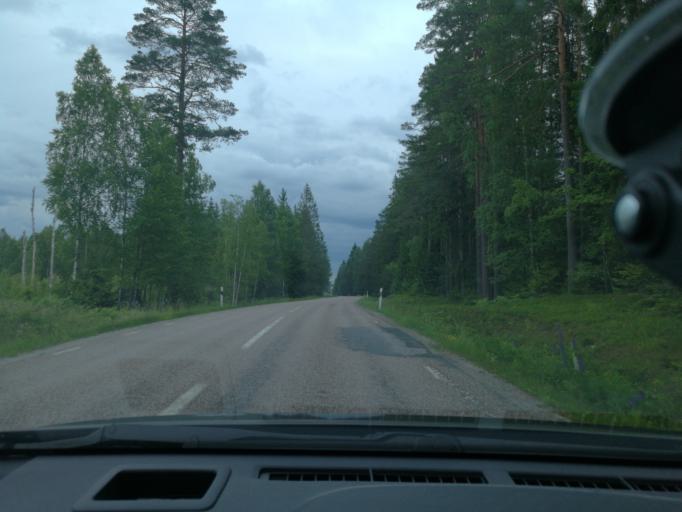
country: SE
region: Vaestmanland
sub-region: Sala Kommun
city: Sala
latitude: 59.9107
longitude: 16.4180
